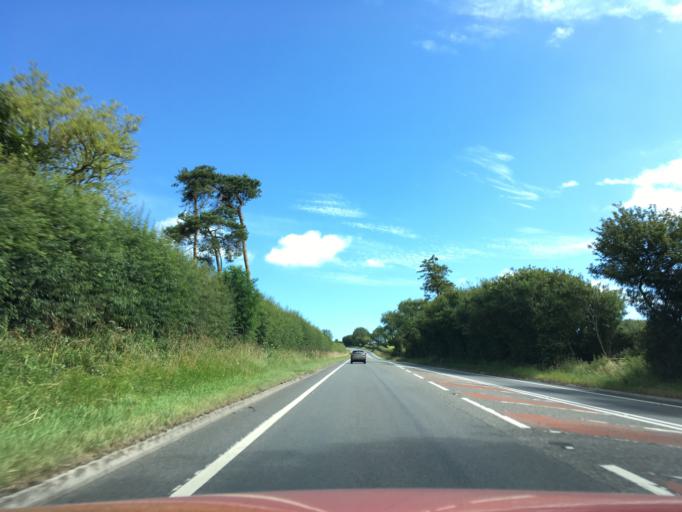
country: GB
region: England
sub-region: Somerset
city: Yeovil
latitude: 50.8332
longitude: -2.5744
